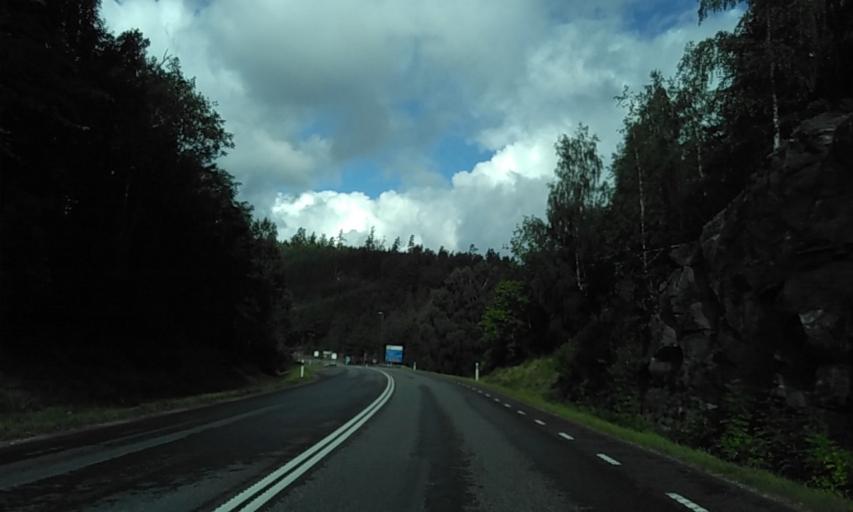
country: SE
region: Vaestra Goetaland
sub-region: Alingsas Kommun
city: Alingsas
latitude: 57.9752
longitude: 12.4371
